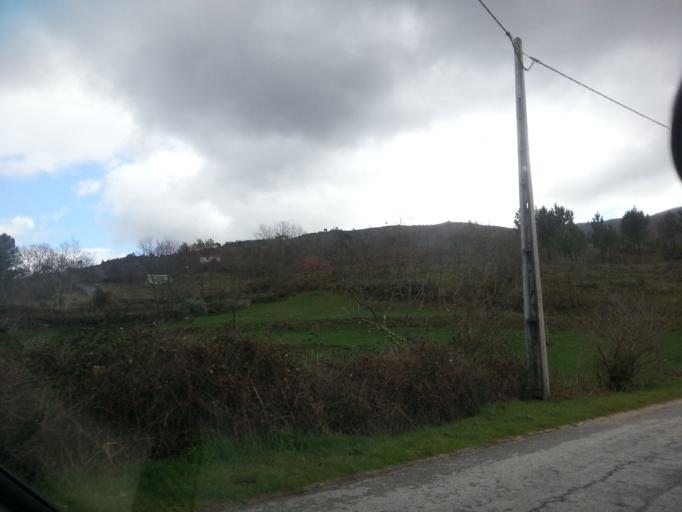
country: PT
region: Guarda
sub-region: Celorico da Beira
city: Celorico da Beira
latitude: 40.5630
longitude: -7.4590
